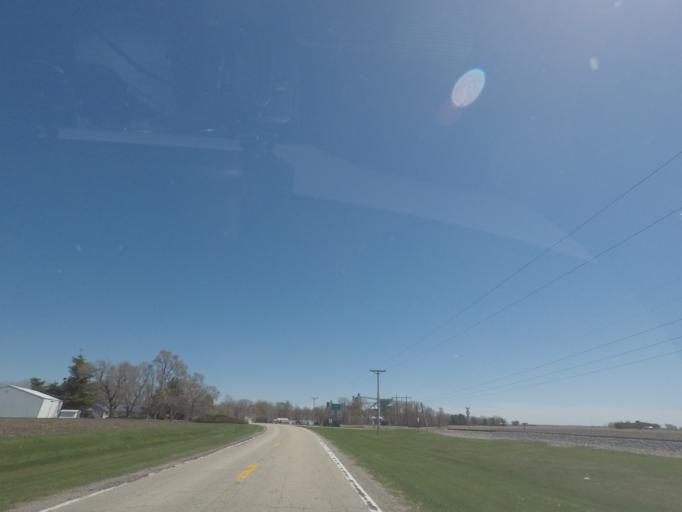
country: US
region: Illinois
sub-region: Macon County
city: Warrensburg
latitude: 39.9688
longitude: -89.1705
